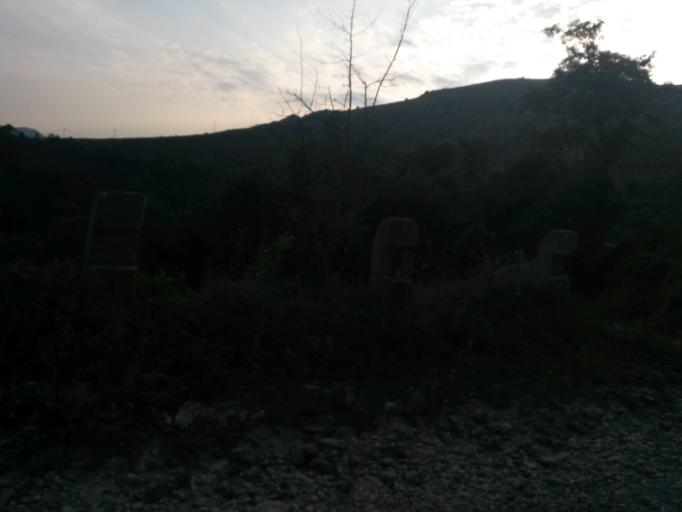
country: RO
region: Alba
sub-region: Comuna Livezile
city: Livezile
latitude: 46.3267
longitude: 23.5362
